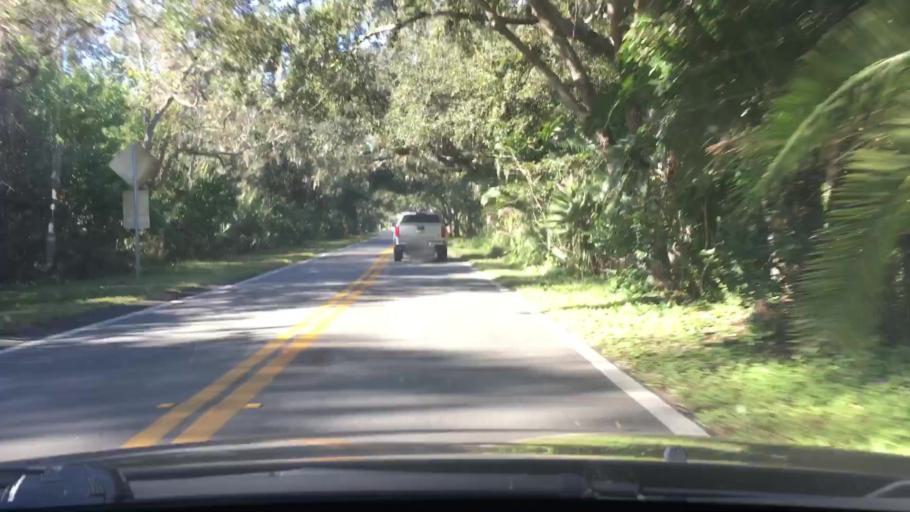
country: US
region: Florida
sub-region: Volusia County
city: Ormond-by-the-Sea
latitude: 29.3496
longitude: -81.0973
